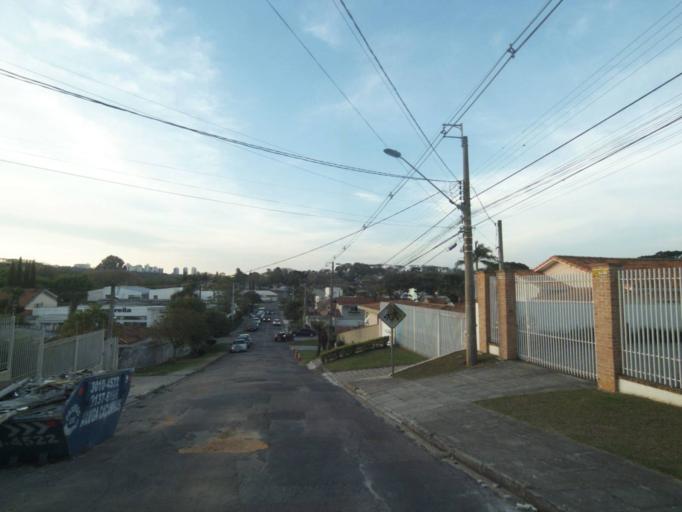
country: BR
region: Parana
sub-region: Curitiba
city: Curitiba
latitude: -25.4555
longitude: -49.3105
